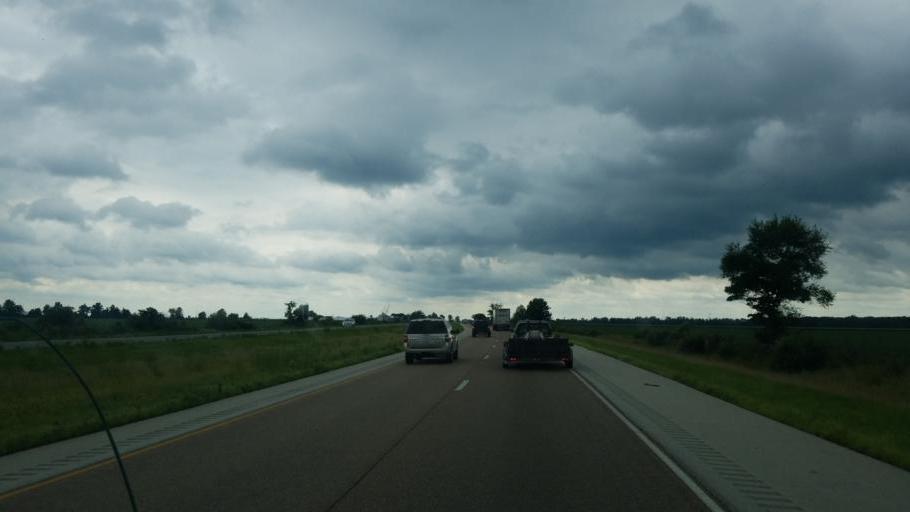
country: US
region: Illinois
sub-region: Effingham County
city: Teutopolis
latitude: 39.1834
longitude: -88.3466
